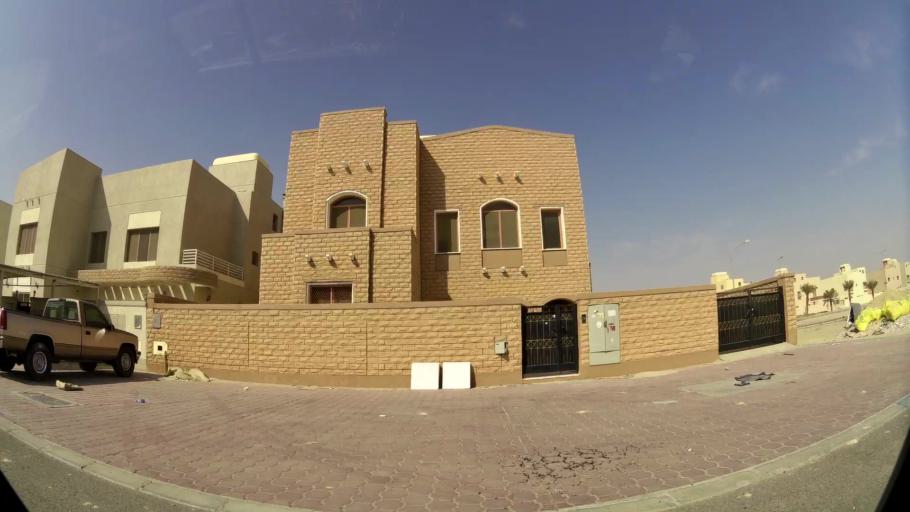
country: KW
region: Al Ahmadi
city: Al Wafrah
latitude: 28.8053
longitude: 48.0636
